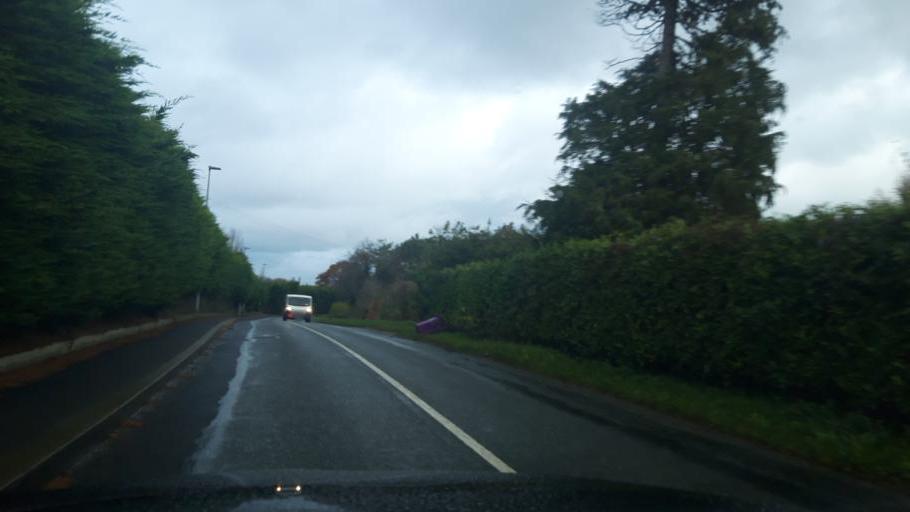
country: IE
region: Leinster
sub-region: Wicklow
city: Kilcoole
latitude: 53.0963
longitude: -6.0678
